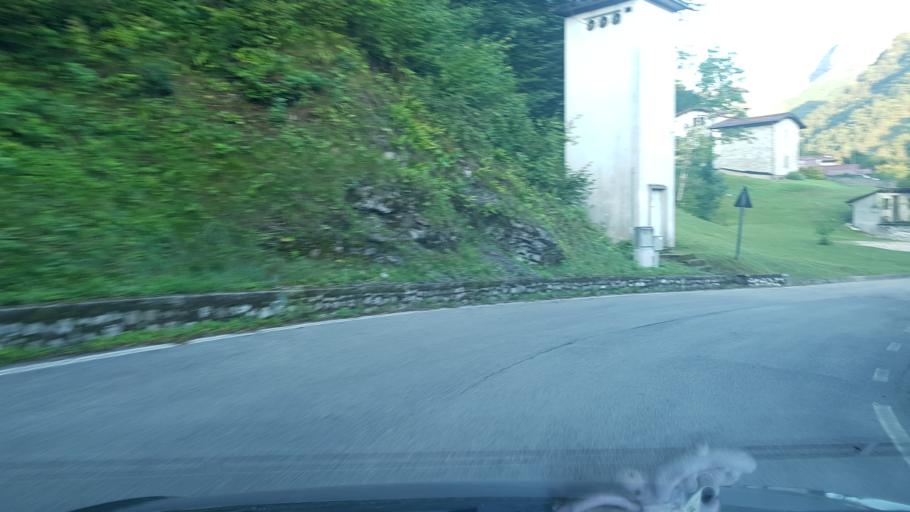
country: IT
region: Friuli Venezia Giulia
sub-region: Provincia di Pordenone
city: Frisanco
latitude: 46.2530
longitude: 12.7405
